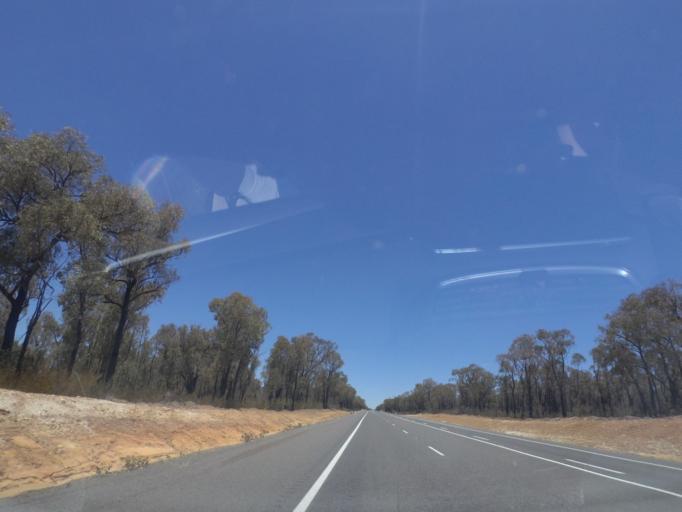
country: AU
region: New South Wales
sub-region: Warrumbungle Shire
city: Coonabarabran
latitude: -30.8960
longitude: 149.4409
